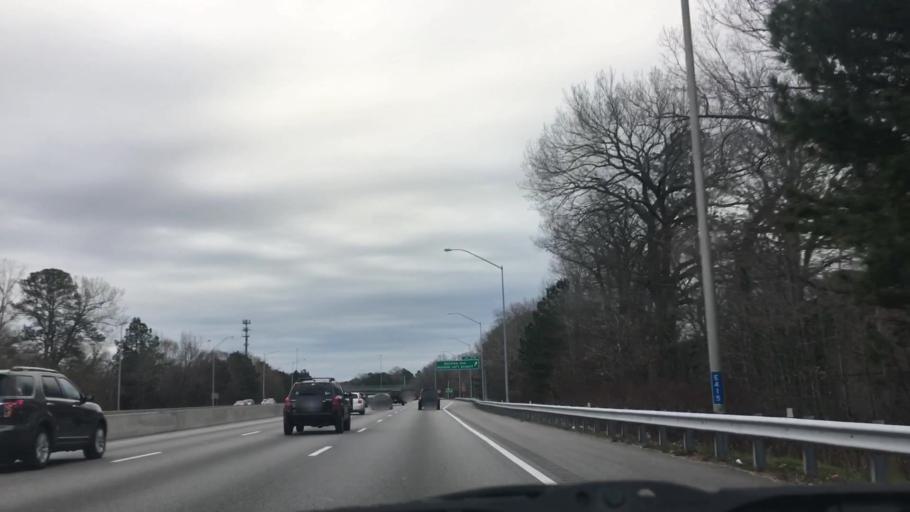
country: US
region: Virginia
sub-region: City of Norfolk
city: Norfolk
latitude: 36.8962
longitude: -76.2337
